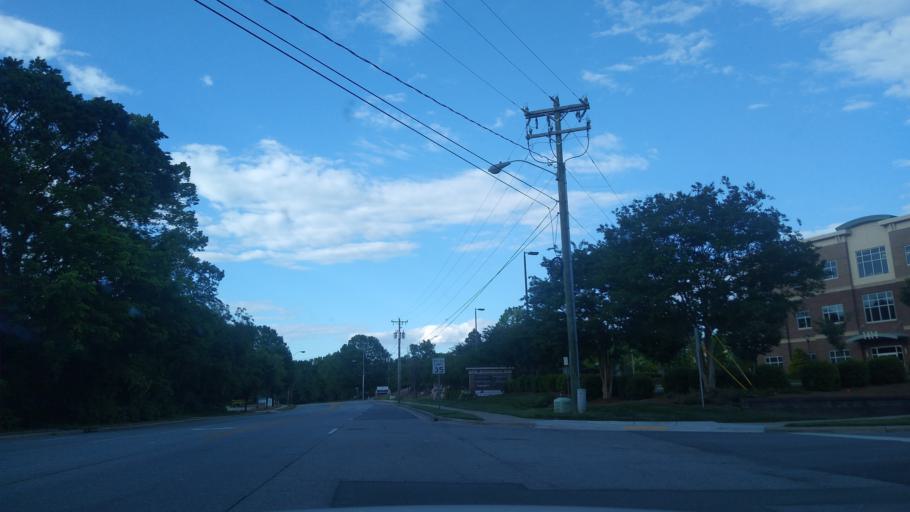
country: US
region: North Carolina
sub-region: Guilford County
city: Greensboro
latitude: 36.0912
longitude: -79.7809
